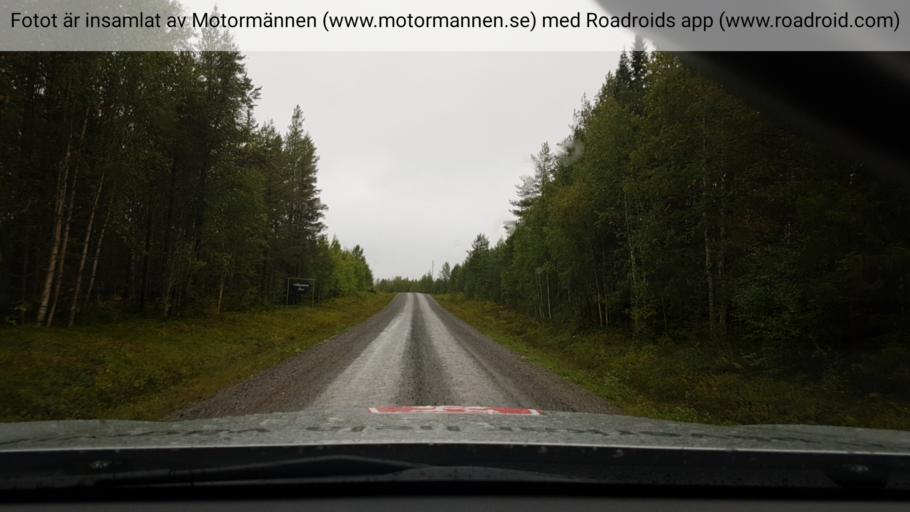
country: SE
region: Vaesterbotten
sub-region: Asele Kommun
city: Asele
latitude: 64.0182
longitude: 17.6465
